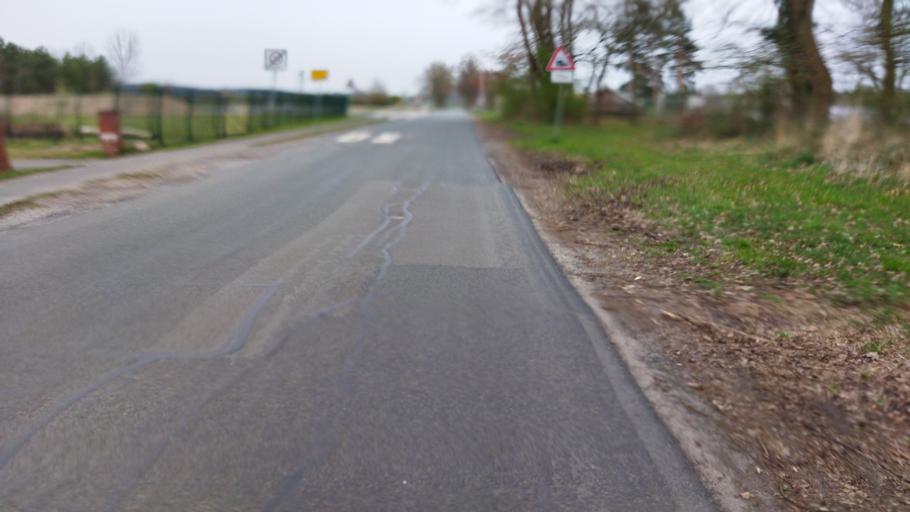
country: DE
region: Lower Saxony
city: Estorf
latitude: 52.5969
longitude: 9.1658
